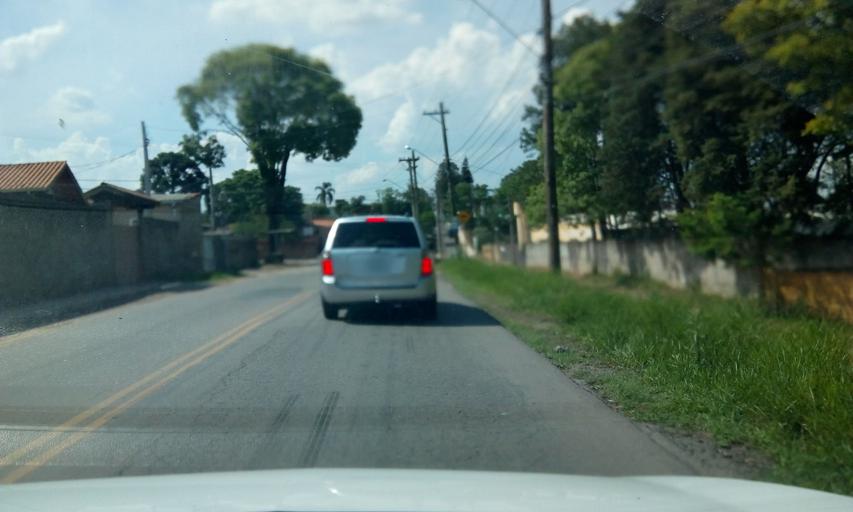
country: BR
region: Sao Paulo
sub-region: Itupeva
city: Itupeva
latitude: -23.1444
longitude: -47.0357
